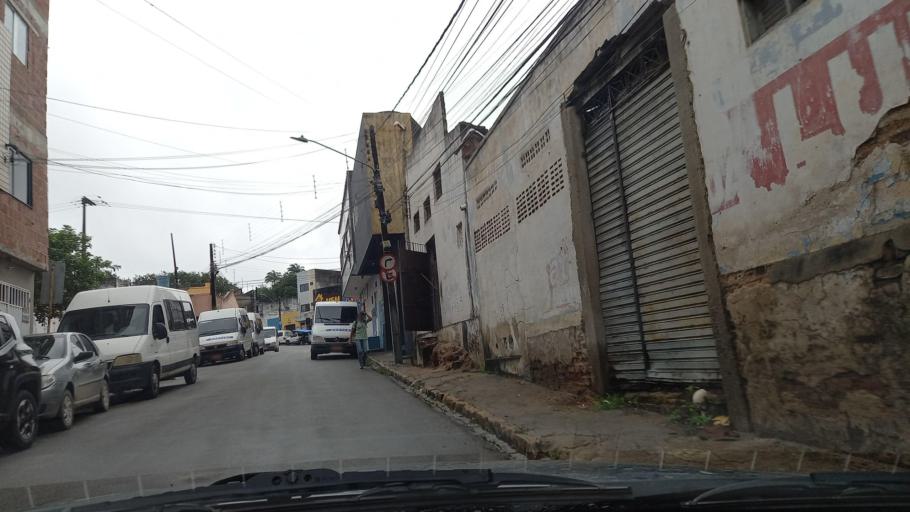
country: BR
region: Pernambuco
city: Garanhuns
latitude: -8.8931
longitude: -36.4938
